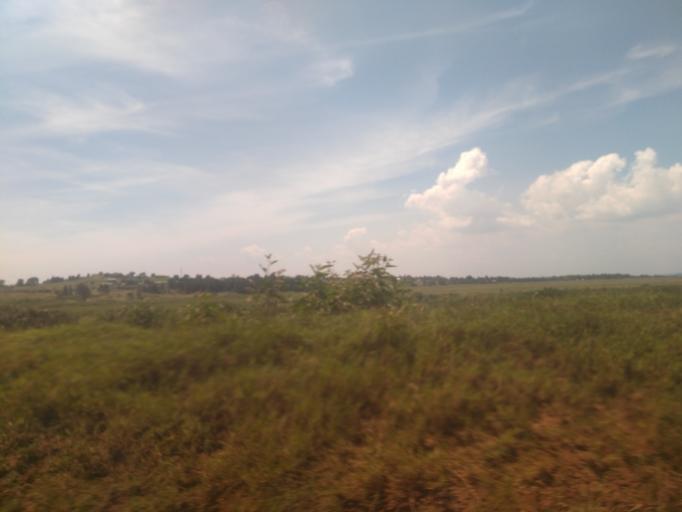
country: UG
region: Central Region
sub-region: Wakiso District
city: Entebbe
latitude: 0.0406
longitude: 32.4369
